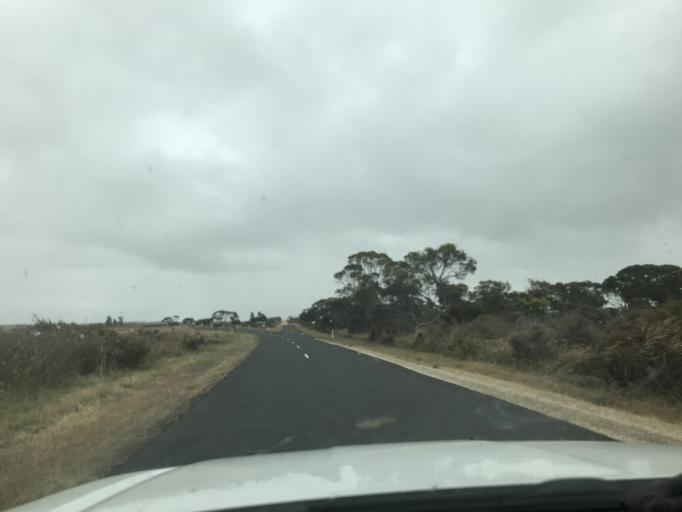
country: AU
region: South Australia
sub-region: Tatiara
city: Bordertown
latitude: -36.1159
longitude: 141.0275
